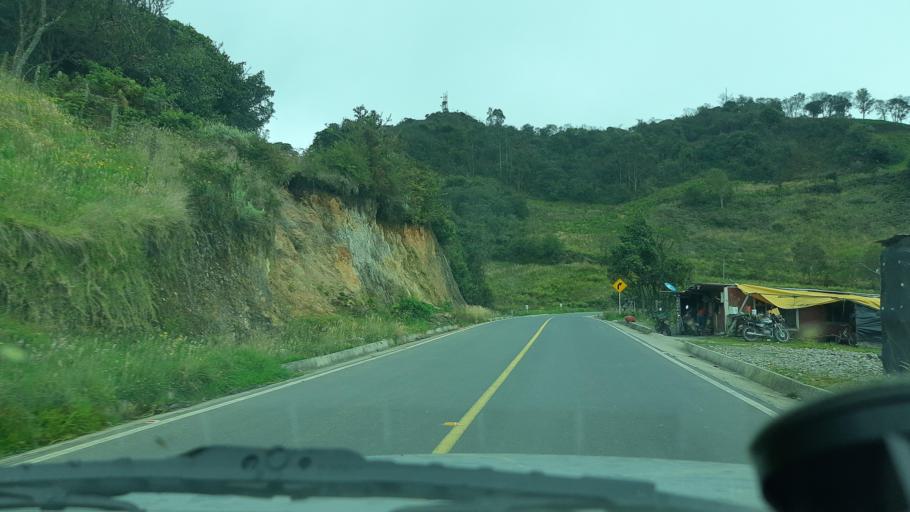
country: CO
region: Cundinamarca
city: Umbita
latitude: 5.2284
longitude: -73.4722
